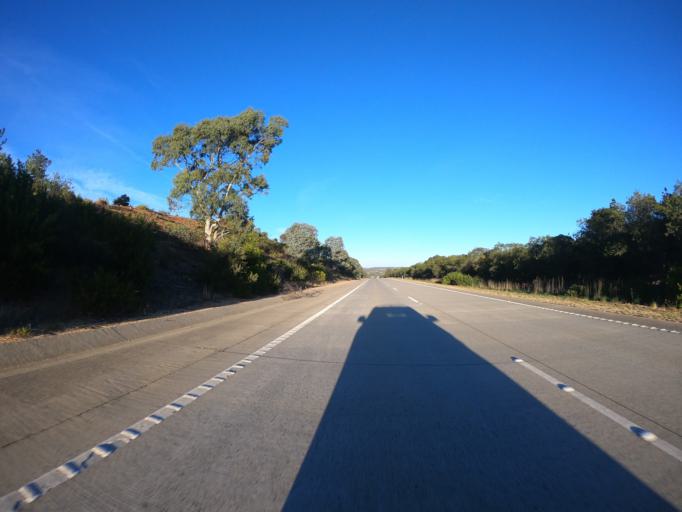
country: AU
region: New South Wales
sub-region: Yass Valley
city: Gundaroo
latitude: -35.1131
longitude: 149.3629
